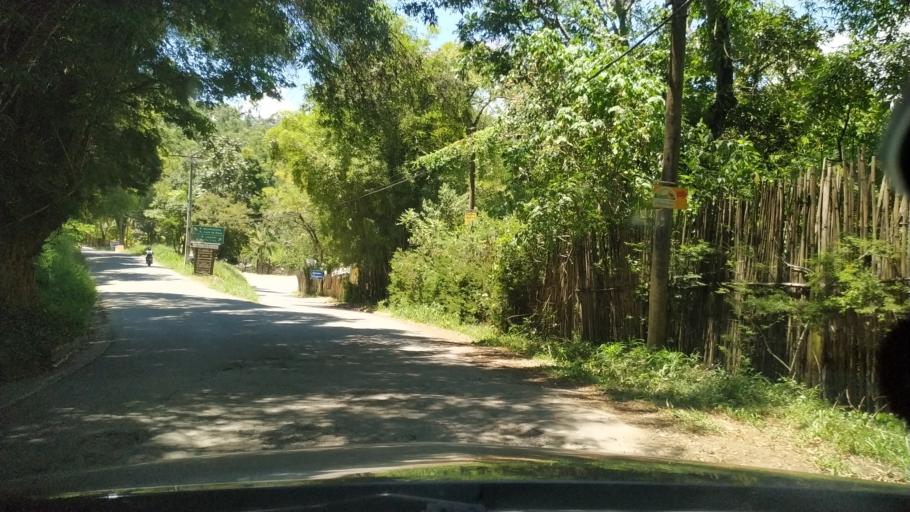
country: BR
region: Sao Paulo
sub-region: Campos Do Jordao
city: Campos do Jordao
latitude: -22.8123
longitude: -45.6825
